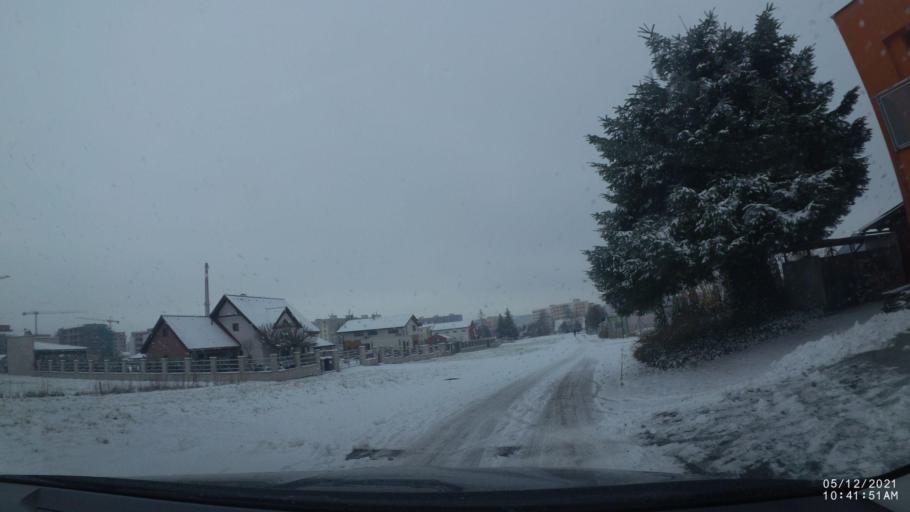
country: CZ
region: Kralovehradecky
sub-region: Okres Rychnov nad Kneznou
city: Rychnov nad Kneznou
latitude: 50.1656
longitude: 16.2873
